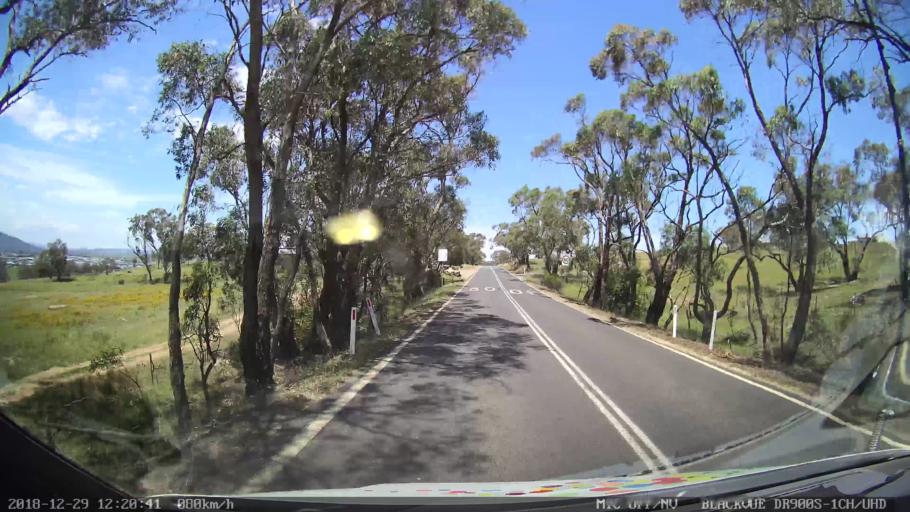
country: AU
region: New South Wales
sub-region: Queanbeyan
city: Queanbeyan
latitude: -35.4059
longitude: 149.2288
